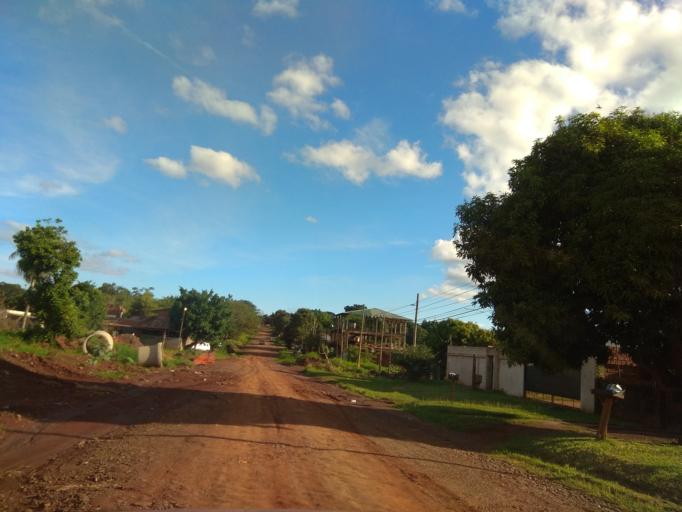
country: AR
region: Misiones
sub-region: Departamento de Capital
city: Posadas
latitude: -27.3942
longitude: -55.9278
